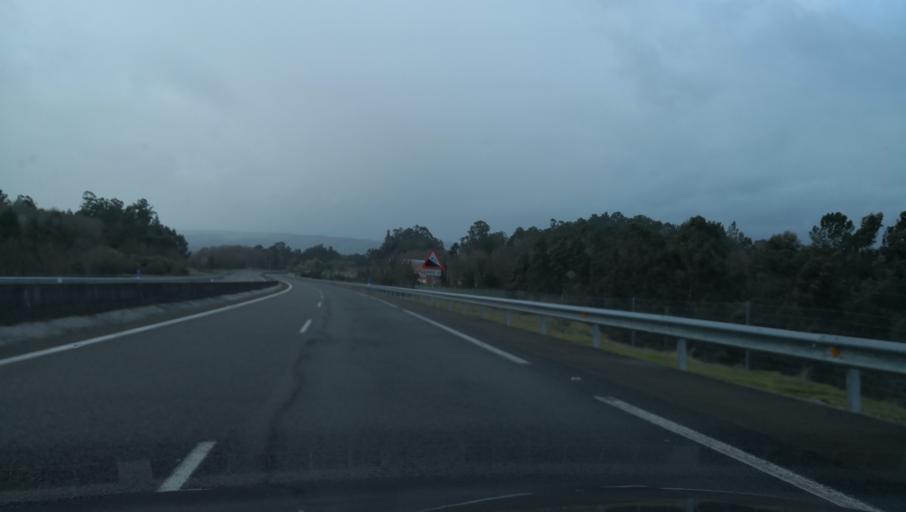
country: ES
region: Galicia
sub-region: Provincia da Coruna
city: Ribeira
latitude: 42.7464
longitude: -8.3799
